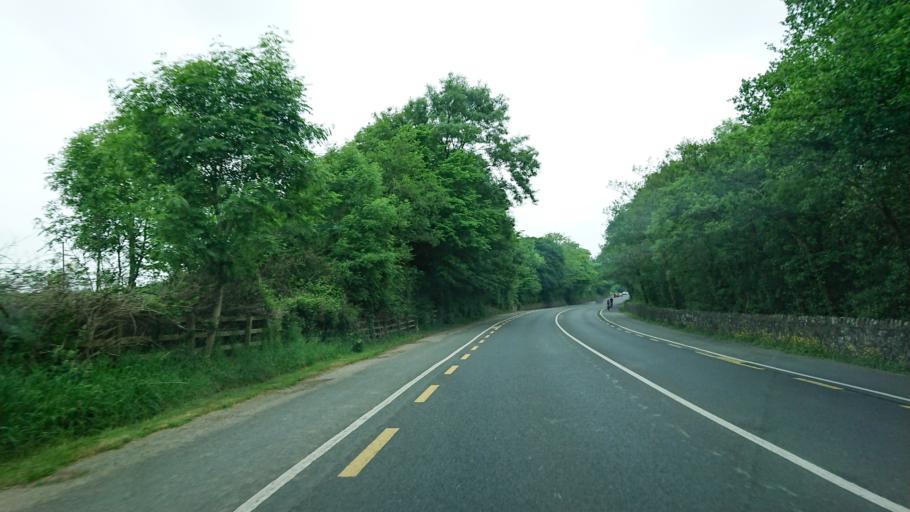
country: IE
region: Munster
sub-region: Waterford
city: Waterford
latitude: 52.2157
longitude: -7.1255
